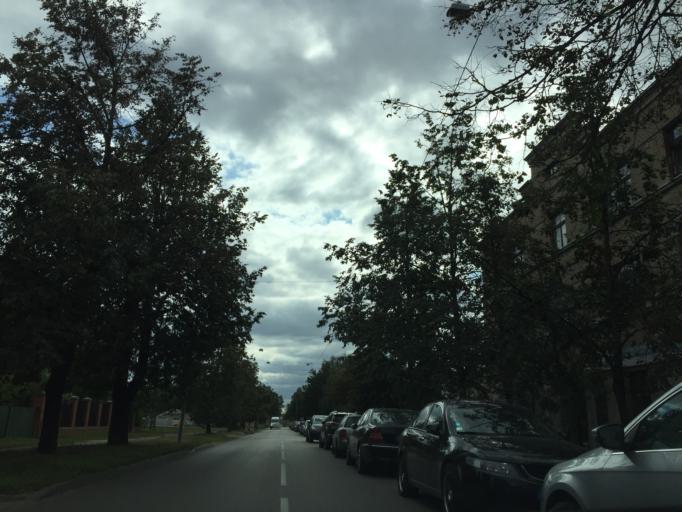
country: LV
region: Riga
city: Riga
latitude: 56.9499
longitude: 24.1542
